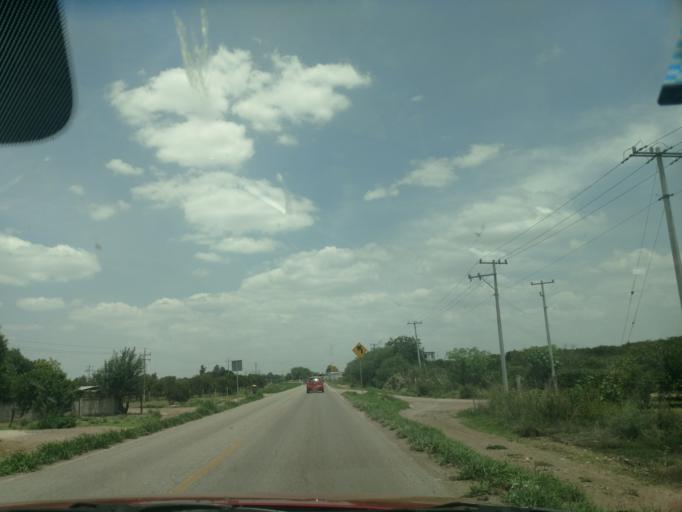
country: MX
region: San Luis Potosi
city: Ciudad Fernandez
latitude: 21.9518
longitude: -100.0655
